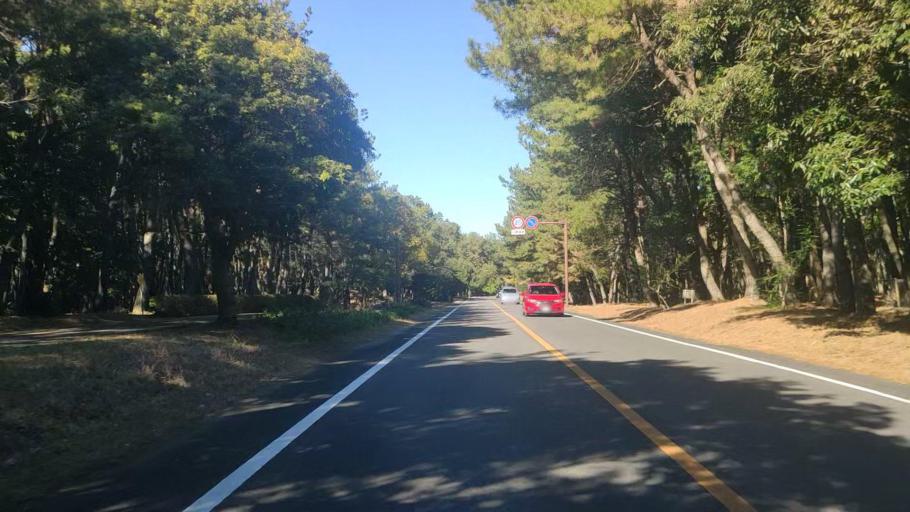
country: JP
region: Miyazaki
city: Miyazaki-shi
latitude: 31.9447
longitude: 131.4648
